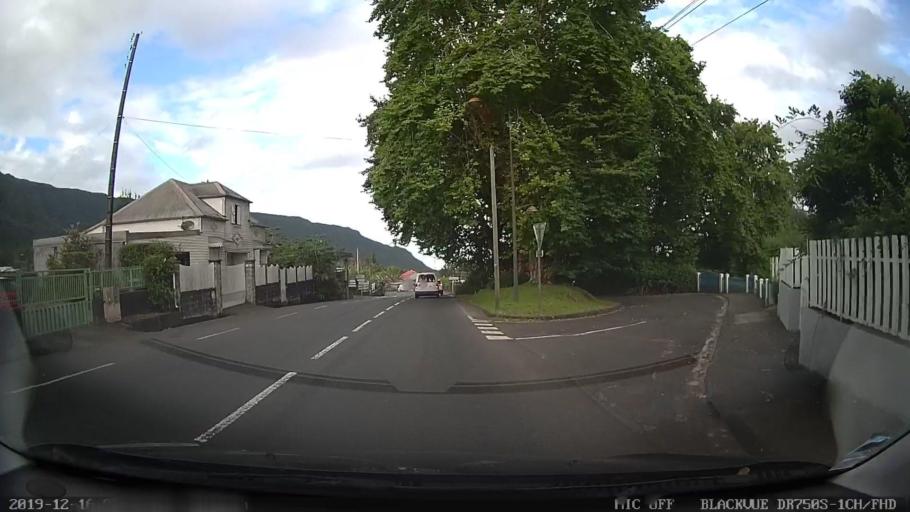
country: RE
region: Reunion
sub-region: Reunion
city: Salazie
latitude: -21.1410
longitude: 55.6221
